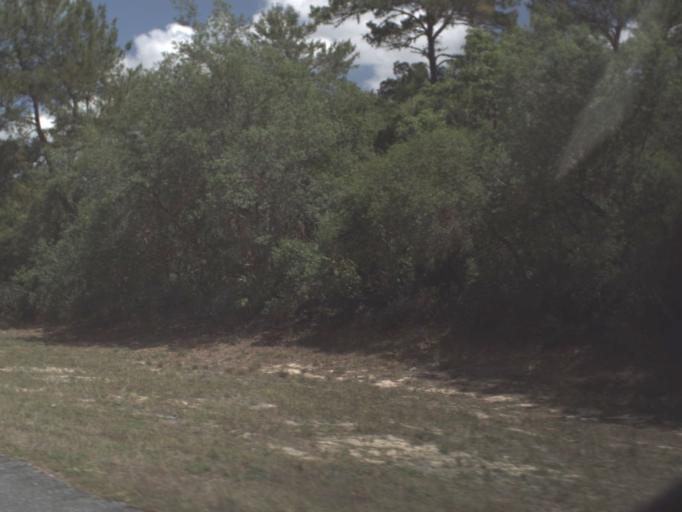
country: US
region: Florida
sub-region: Lake County
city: Astor
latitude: 29.1762
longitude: -81.6997
